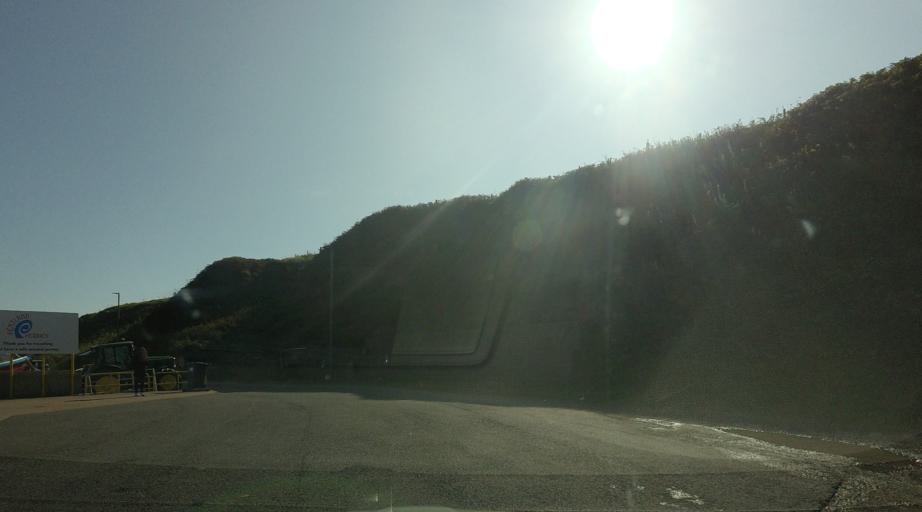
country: GB
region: Scotland
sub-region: Highland
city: Wick
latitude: 58.6381
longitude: -3.1622
